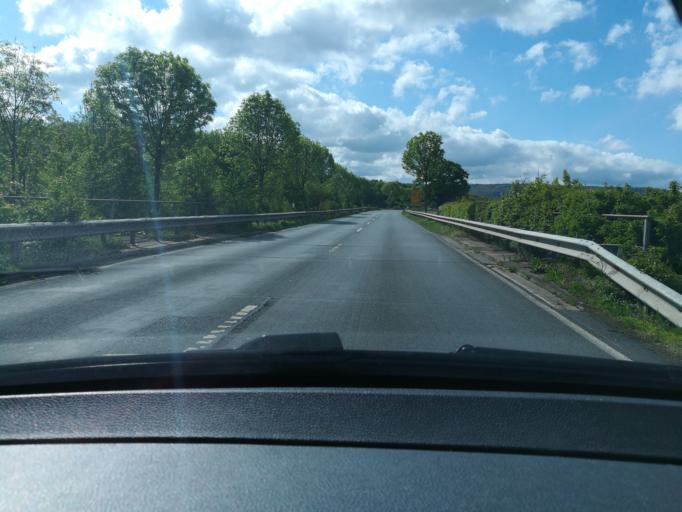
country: DE
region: North Rhine-Westphalia
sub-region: Regierungsbezirk Detmold
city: Minden
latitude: 52.2755
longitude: 8.9269
